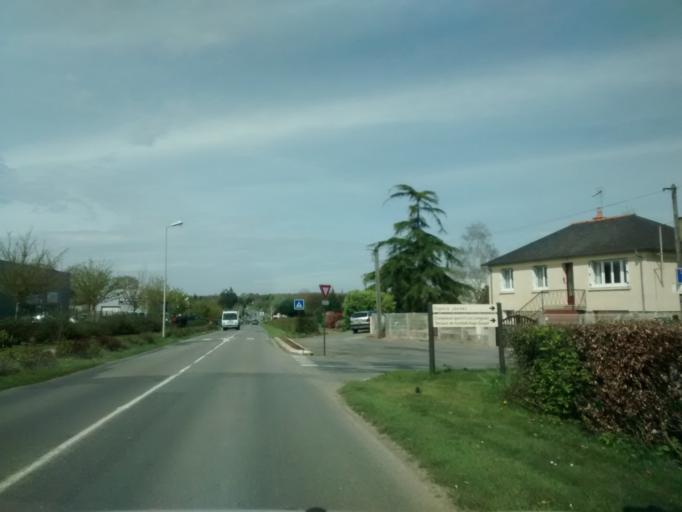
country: FR
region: Brittany
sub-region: Departement d'Ille-et-Vilaine
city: Fouillard
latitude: 48.1524
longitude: -1.5865
